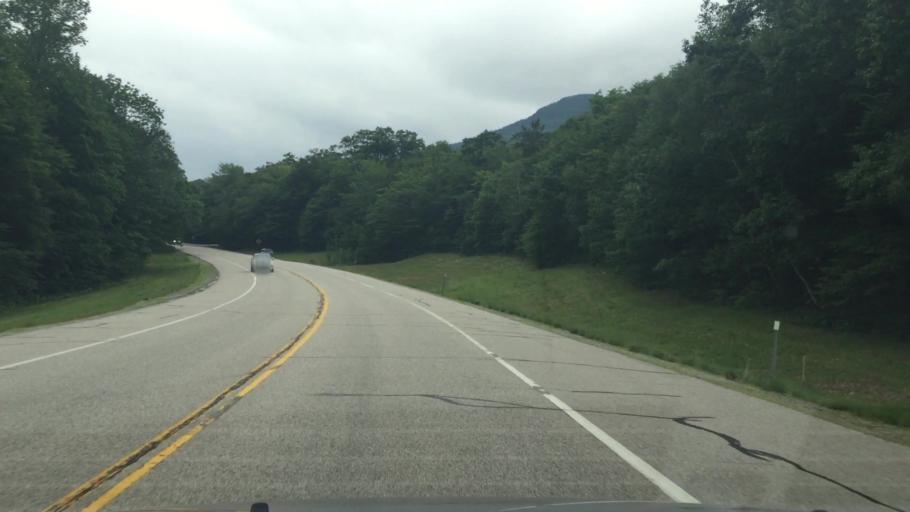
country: US
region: New Hampshire
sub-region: Carroll County
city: North Conway
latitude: 44.1507
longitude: -71.3662
